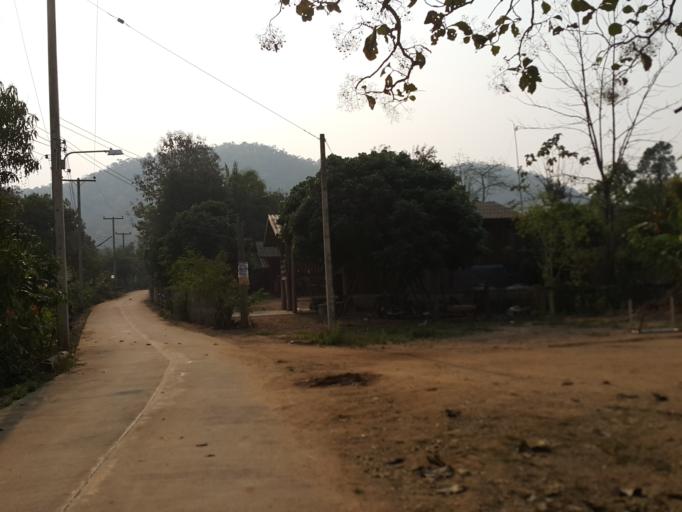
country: TH
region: Lamphun
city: Li
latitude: 17.6051
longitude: 98.9664
